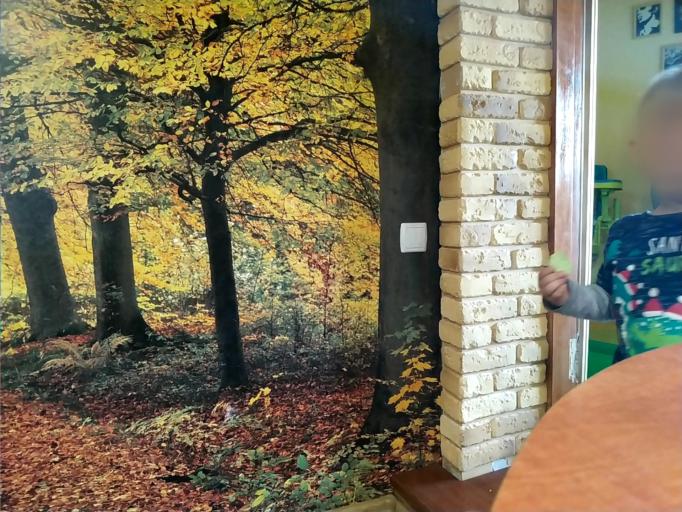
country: RU
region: Leningrad
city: Luga
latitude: 58.9686
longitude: 29.5539
